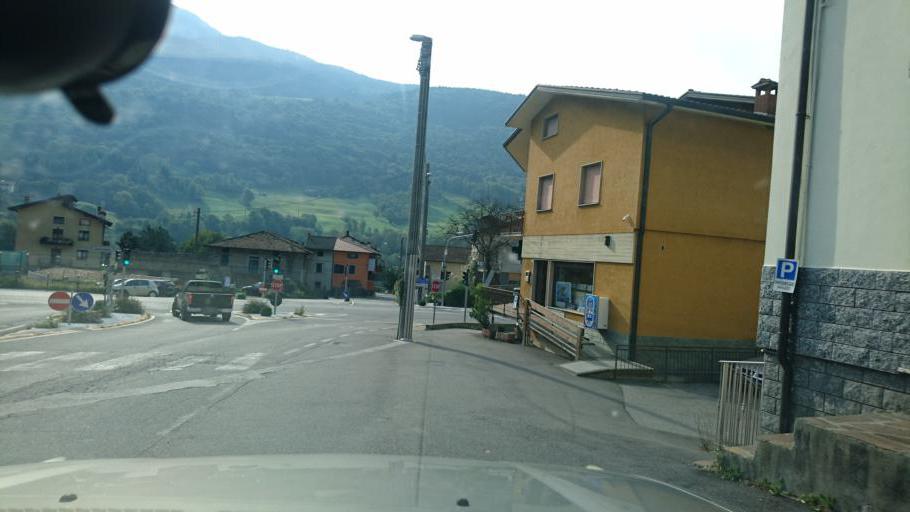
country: IT
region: Lombardy
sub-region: Provincia di Brescia
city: Malonno
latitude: 46.1203
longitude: 10.3196
